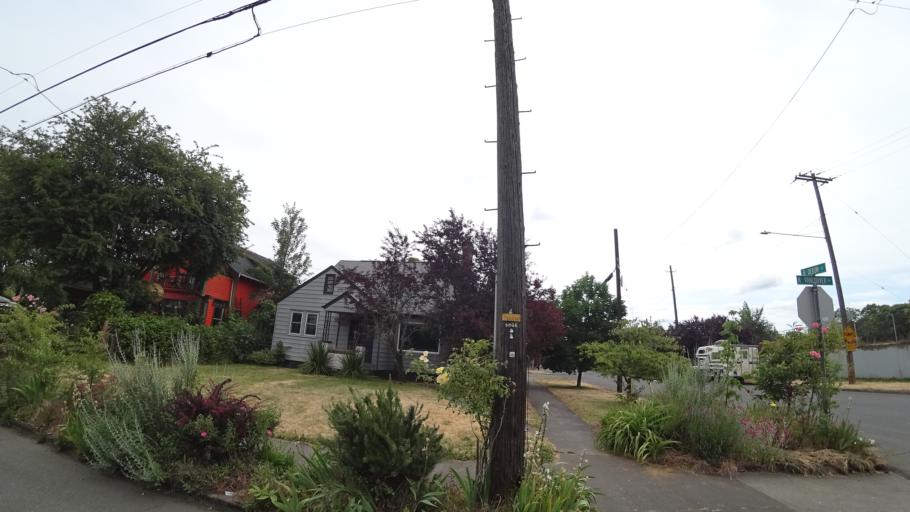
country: US
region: Oregon
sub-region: Multnomah County
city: Portland
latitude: 45.5719
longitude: -122.6688
